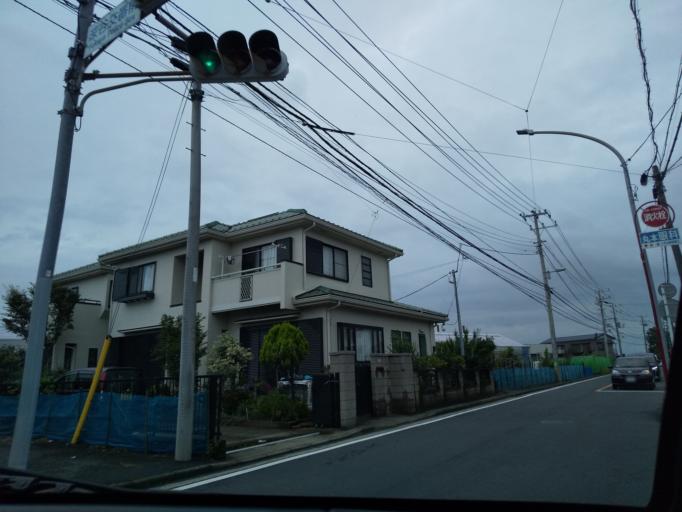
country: JP
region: Kanagawa
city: Fujisawa
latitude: 35.3928
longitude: 139.5058
